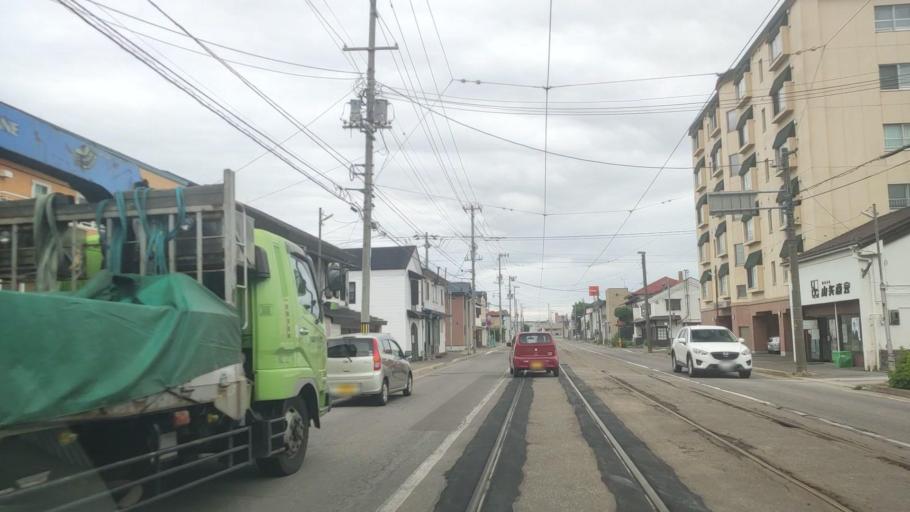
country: JP
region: Hokkaido
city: Hakodate
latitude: 41.7715
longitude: 140.7069
